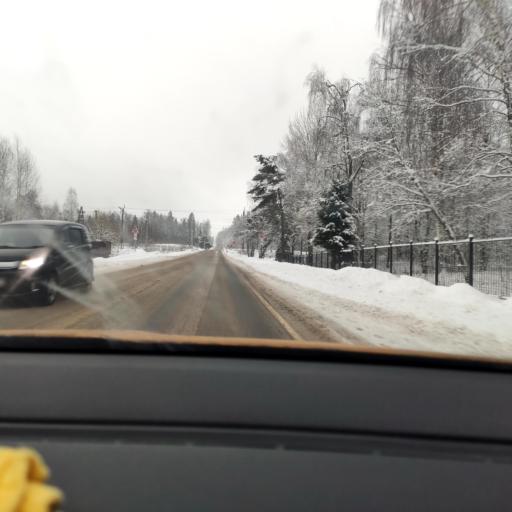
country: RU
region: Moskovskaya
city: Yershovo
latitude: 55.7716
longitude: 36.8024
